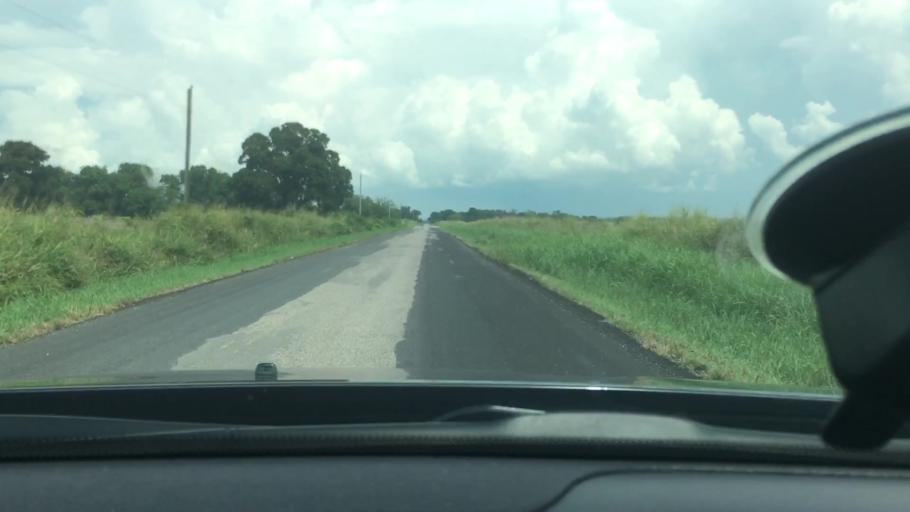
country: US
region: Oklahoma
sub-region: Carter County
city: Dickson
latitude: 34.2058
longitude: -96.8982
